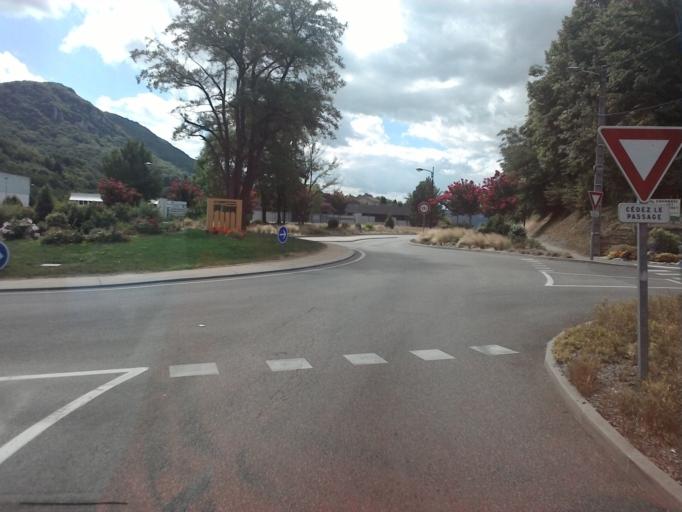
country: FR
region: Rhone-Alpes
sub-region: Departement de l'Ain
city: Lagnieu
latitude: 45.9087
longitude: 5.3466
